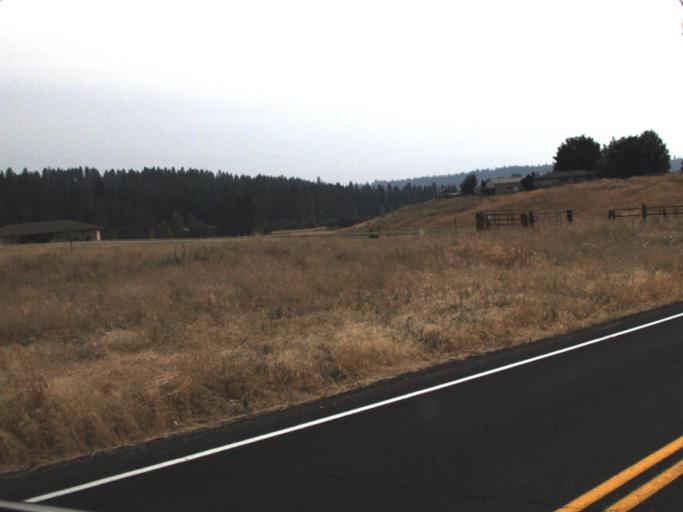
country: US
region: Washington
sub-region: Spokane County
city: Trentwood
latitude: 47.7951
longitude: -117.2459
